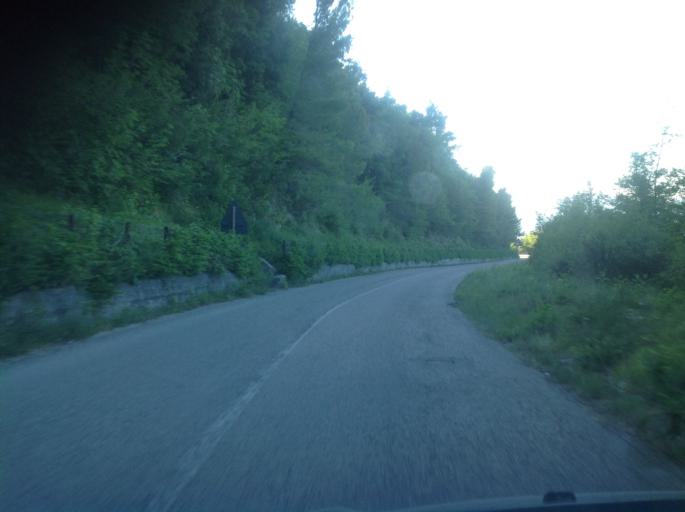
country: IT
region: Umbria
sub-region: Provincia di Terni
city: Stroncone
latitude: 42.4838
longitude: 12.6665
